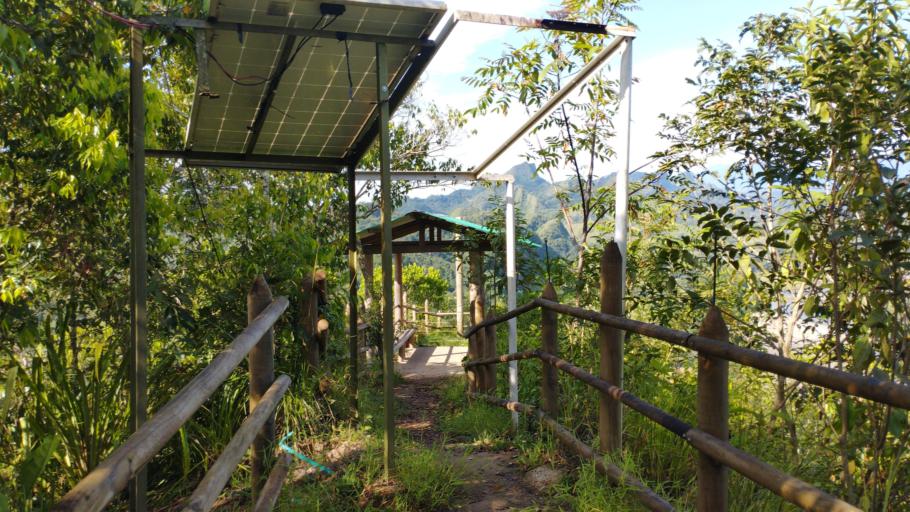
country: CO
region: Boyaca
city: San Luis de Gaceno
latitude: 4.8182
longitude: -73.1609
